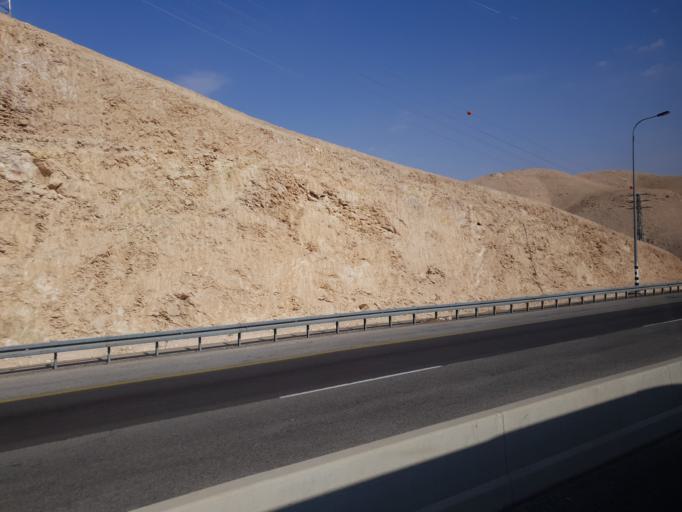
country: PS
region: West Bank
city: Jericho
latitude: 31.8159
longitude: 35.3710
